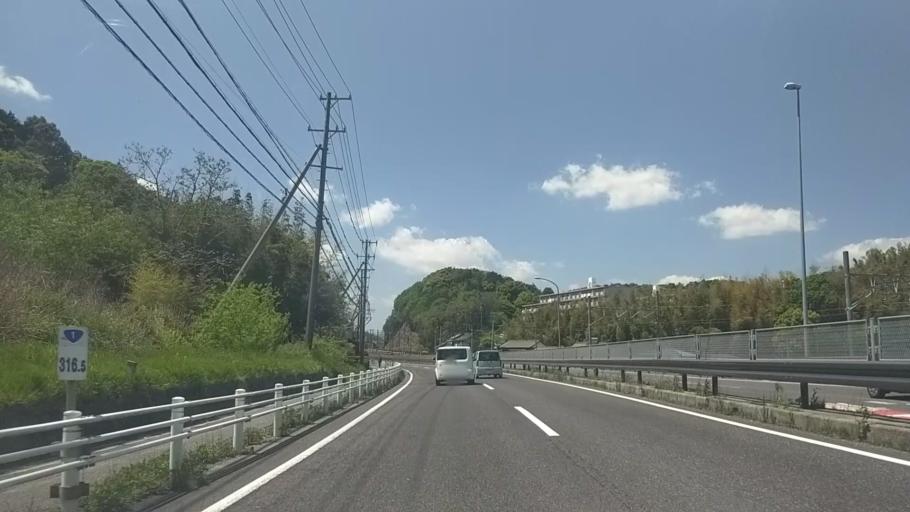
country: JP
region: Aichi
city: Gamagori
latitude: 34.8975
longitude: 137.2484
